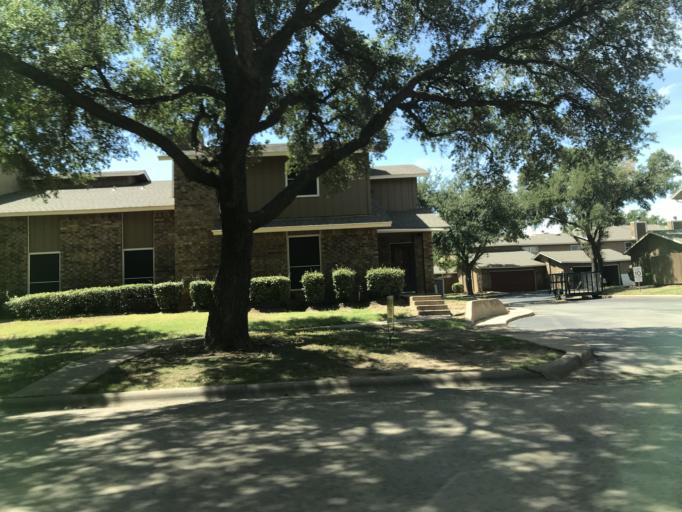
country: US
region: Texas
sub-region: Taylor County
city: Abilene
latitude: 32.4210
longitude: -99.7623
